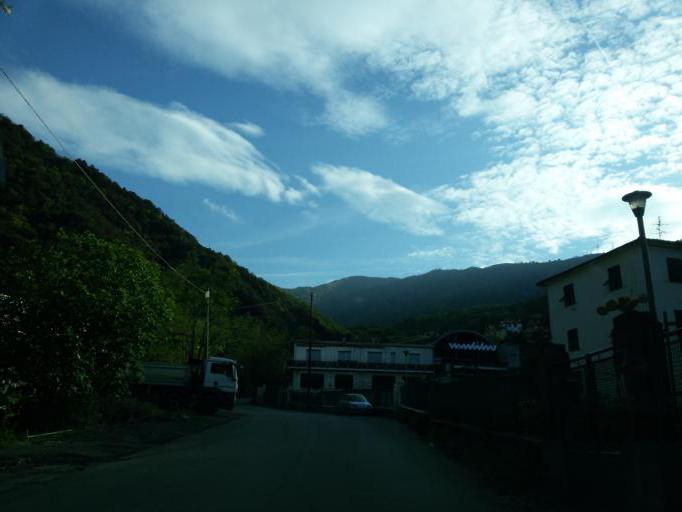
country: IT
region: Liguria
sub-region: Provincia di Genova
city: Piccarello
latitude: 44.4666
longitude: 8.9879
